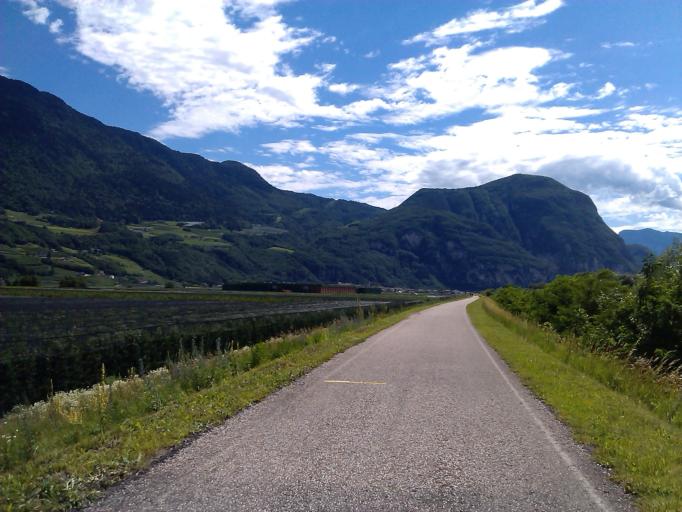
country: IT
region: Trentino-Alto Adige
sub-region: Bolzano
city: Cortina sulla Strada del Vino
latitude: 46.2634
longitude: 11.2298
